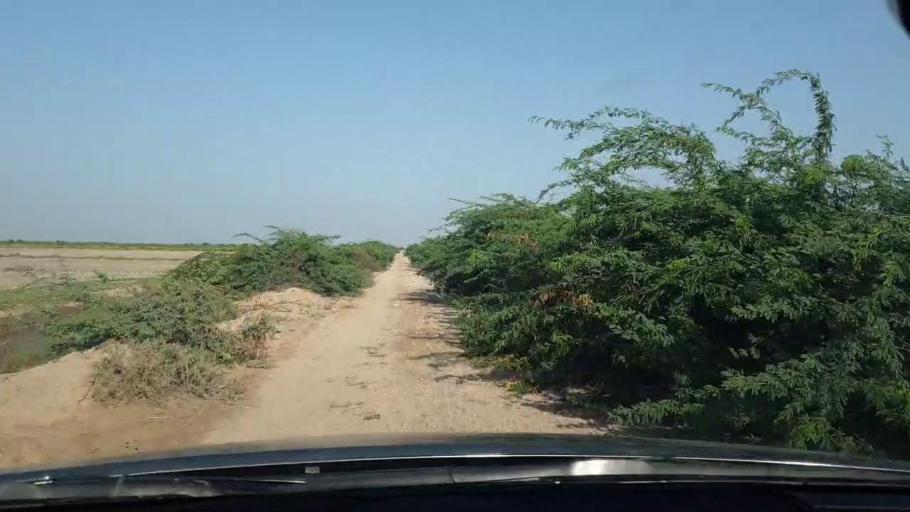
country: PK
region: Sindh
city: Naukot
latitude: 24.8336
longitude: 69.2471
